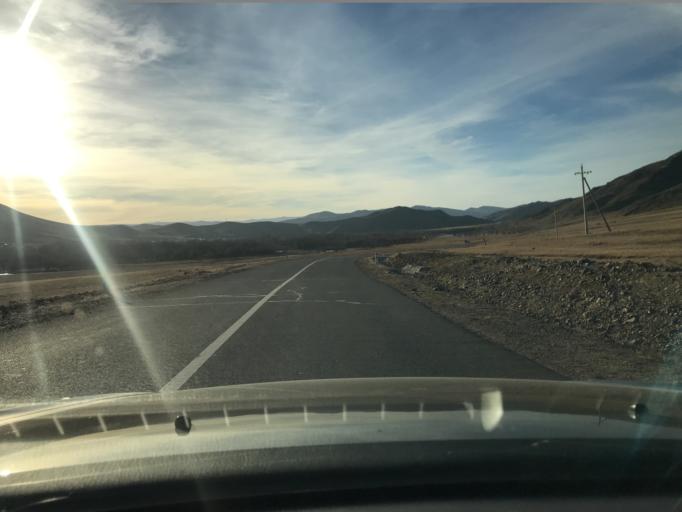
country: MN
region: Central Aimak
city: Dzuunmod
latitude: 47.8214
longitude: 107.3644
